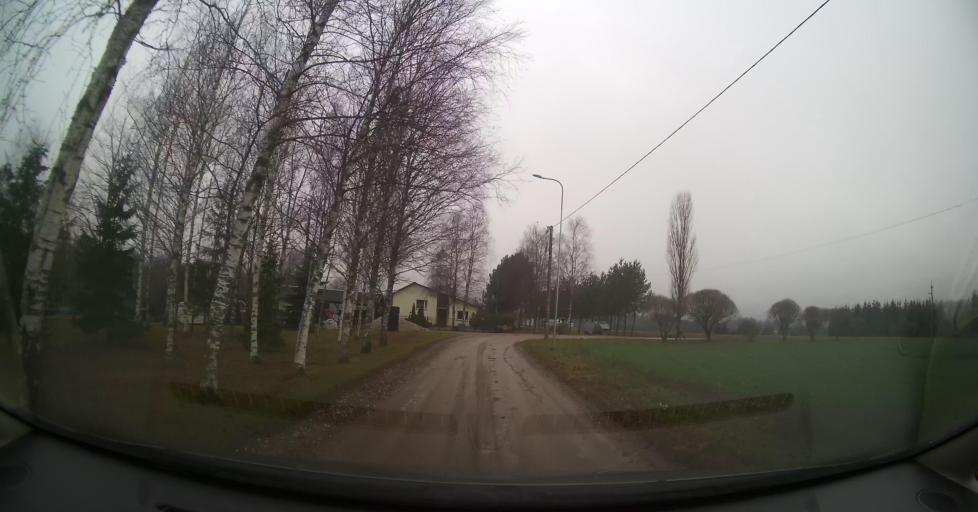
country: EE
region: Tartu
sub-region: Alatskivi vald
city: Kallaste
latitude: 58.3802
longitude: 27.0347
